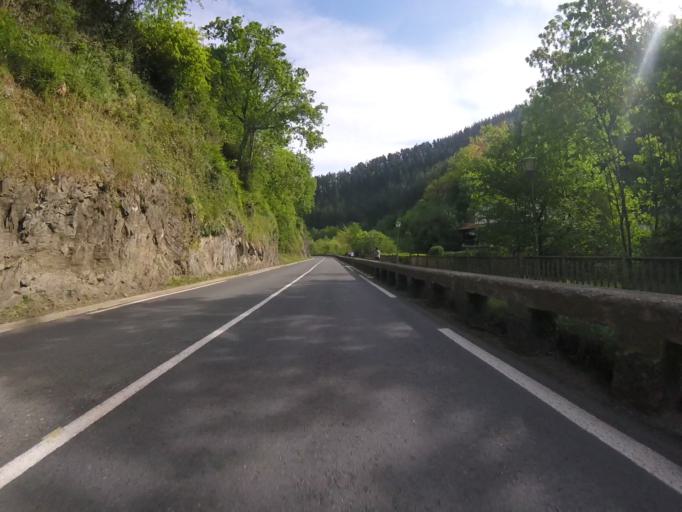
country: ES
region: Basque Country
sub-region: Provincia de Guipuzcoa
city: Urretxu
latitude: 43.1023
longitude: -2.3175
